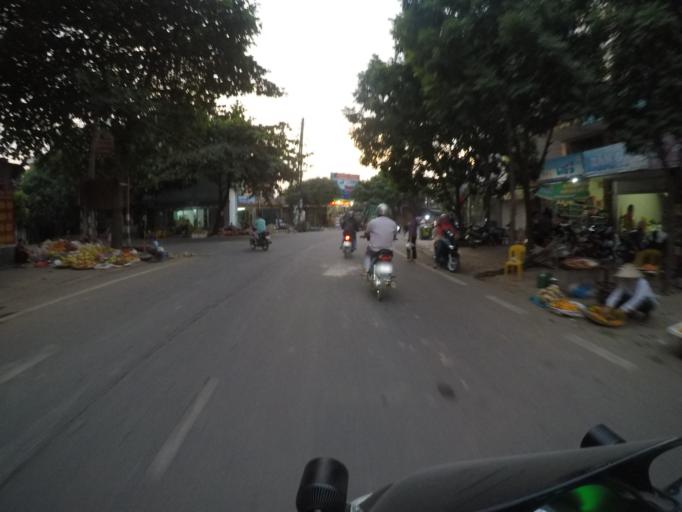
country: VN
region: Vinh Phuc
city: Phuc Yen
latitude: 21.2787
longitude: 105.7325
